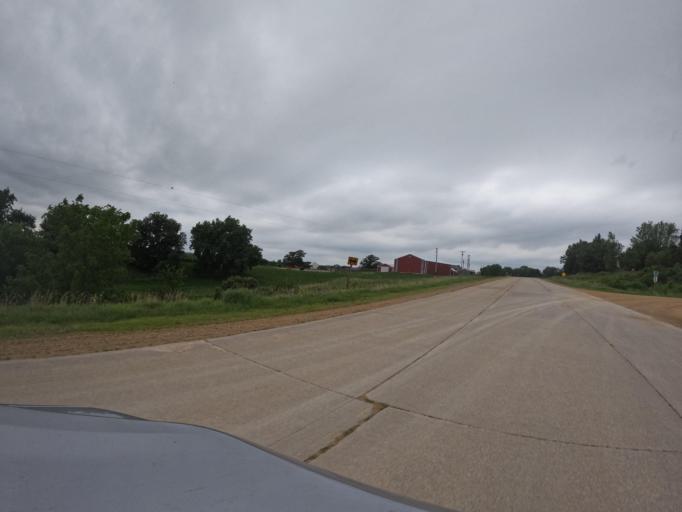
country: US
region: Iowa
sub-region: Jackson County
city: Maquoketa
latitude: 41.9451
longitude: -90.6204
